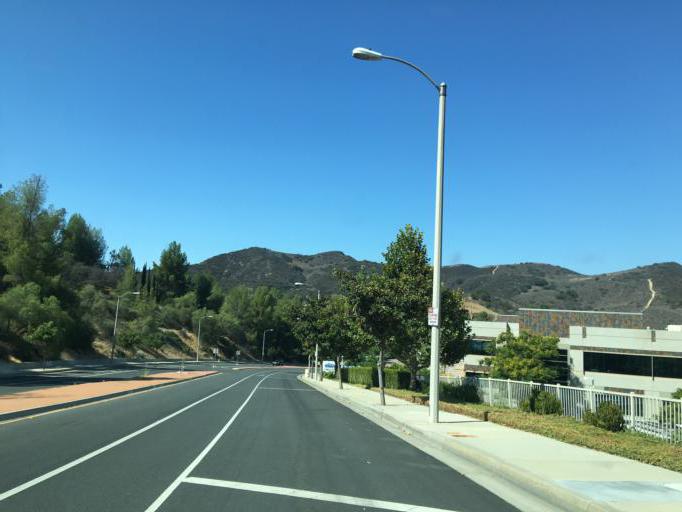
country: US
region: California
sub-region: Los Angeles County
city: Agoura
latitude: 34.1379
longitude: -118.7214
